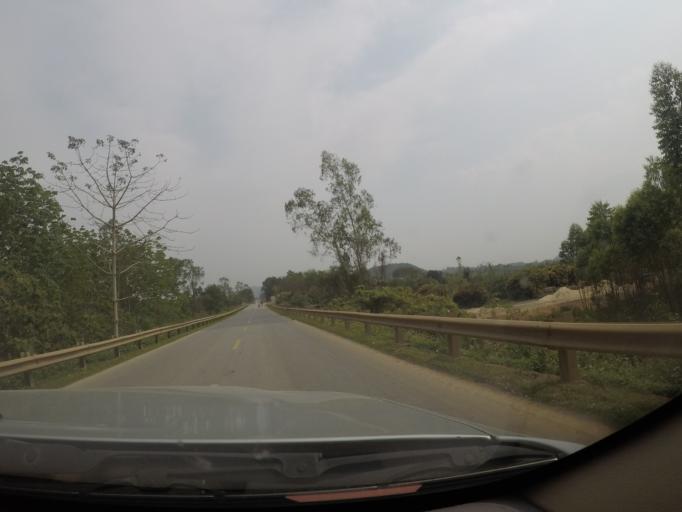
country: VN
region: Nghe An
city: Cau Giat
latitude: 19.3545
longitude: 105.4699
